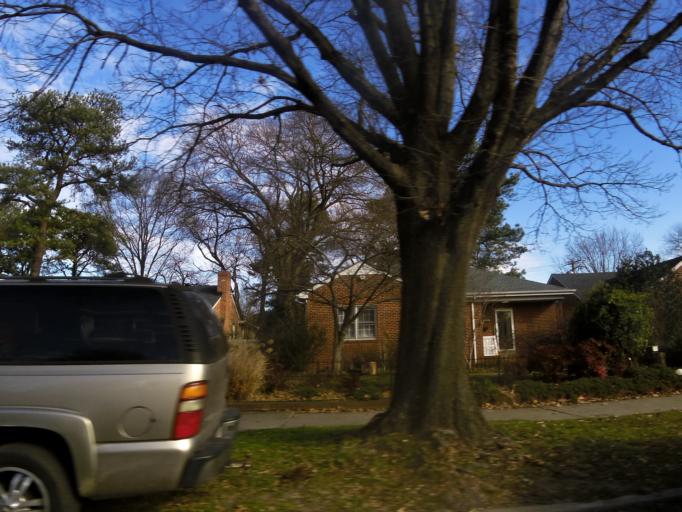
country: US
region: Virginia
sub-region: City of Richmond
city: Richmond
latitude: 37.5683
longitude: -77.4840
